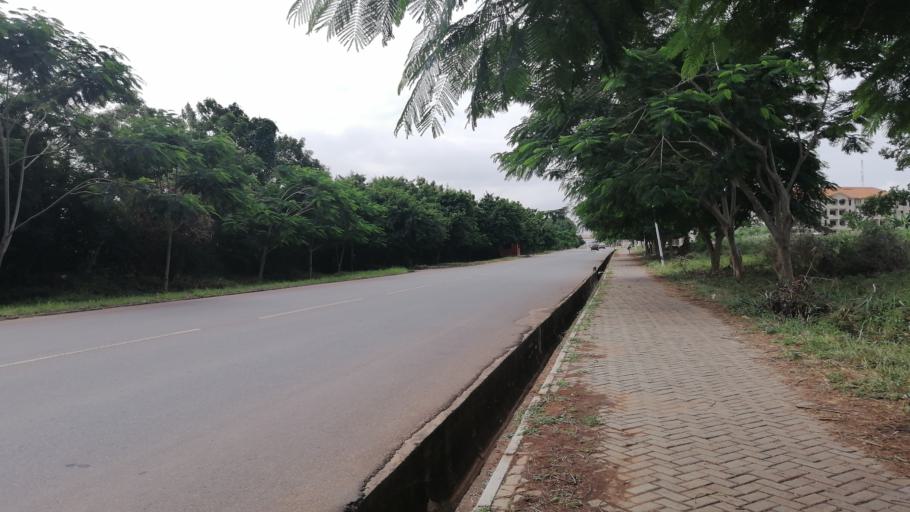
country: GH
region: Greater Accra
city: Medina Estates
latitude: 5.6608
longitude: -0.1826
